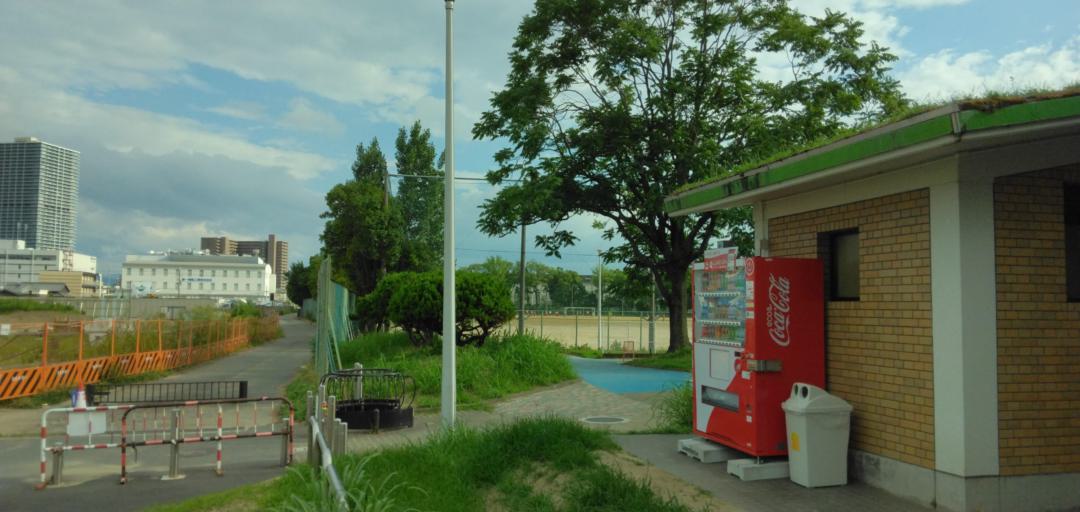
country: JP
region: Osaka
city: Yao
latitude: 34.6287
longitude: 135.5818
